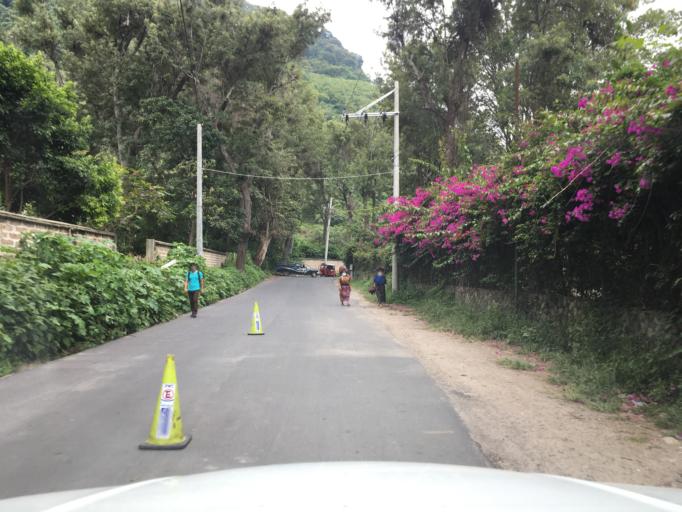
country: GT
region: Solola
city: Panajachel
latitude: 14.7365
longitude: -91.1492
